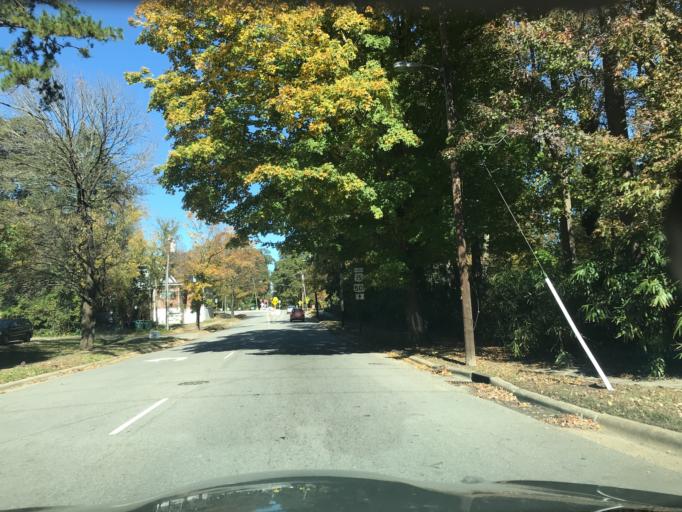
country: US
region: North Carolina
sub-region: Durham County
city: Durham
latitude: 36.0086
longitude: -78.8920
